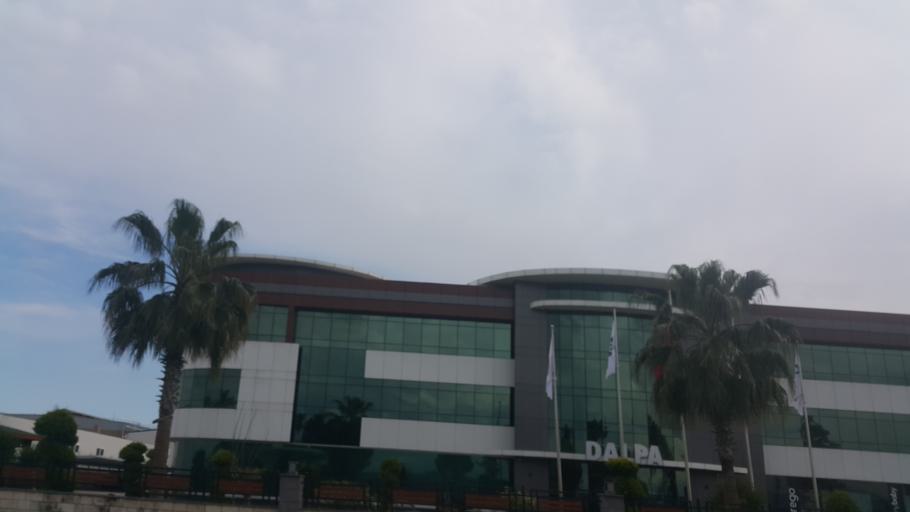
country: TR
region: Mersin
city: Yenice
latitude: 36.9866
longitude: 35.1332
